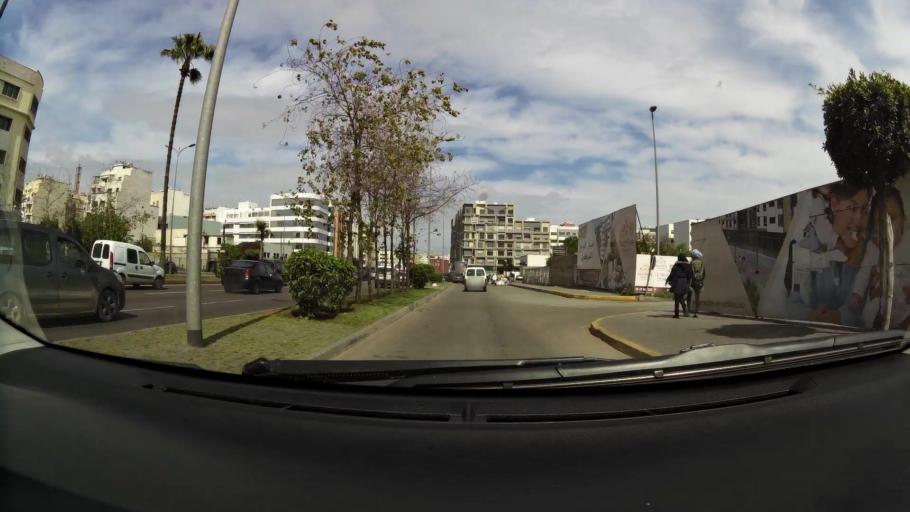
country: MA
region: Grand Casablanca
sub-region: Casablanca
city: Casablanca
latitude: 33.5837
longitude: -7.5962
